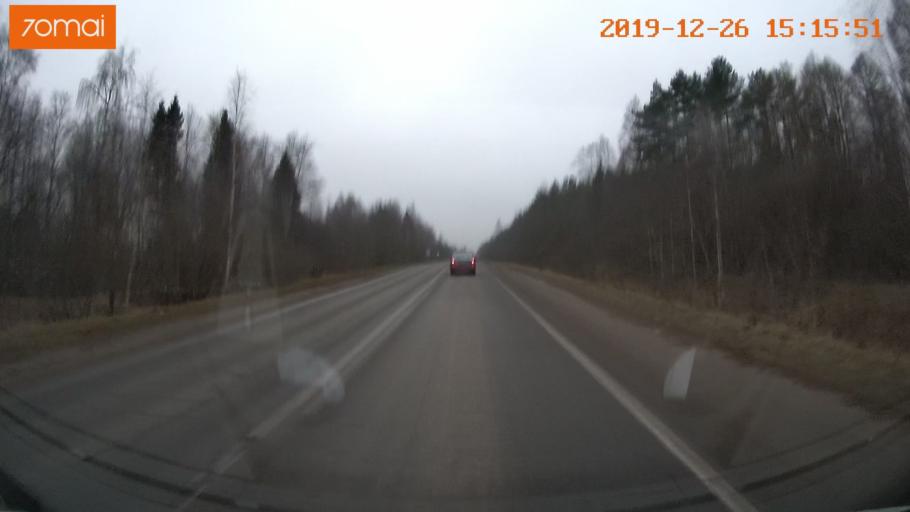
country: RU
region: Jaroslavl
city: Rybinsk
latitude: 58.0926
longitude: 38.8735
